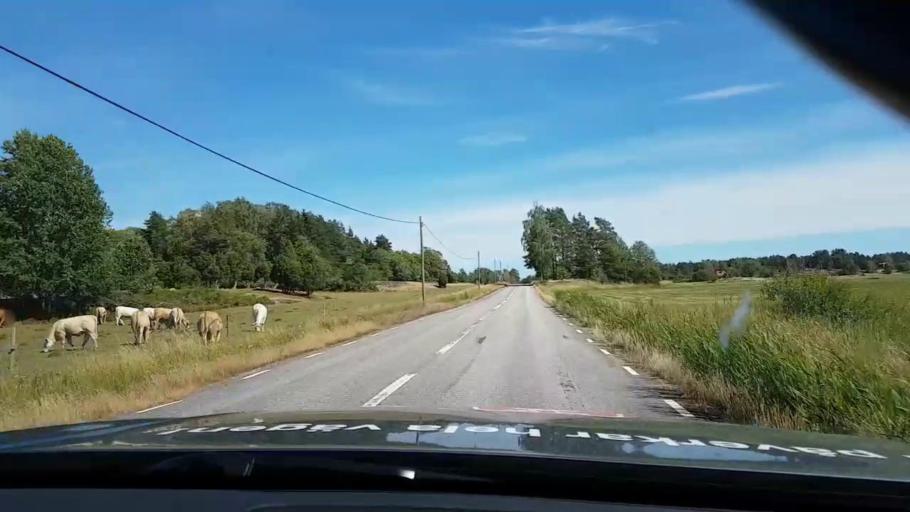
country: SE
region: Kalmar
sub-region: Vasterviks Kommun
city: Forserum
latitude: 57.9321
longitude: 16.5125
